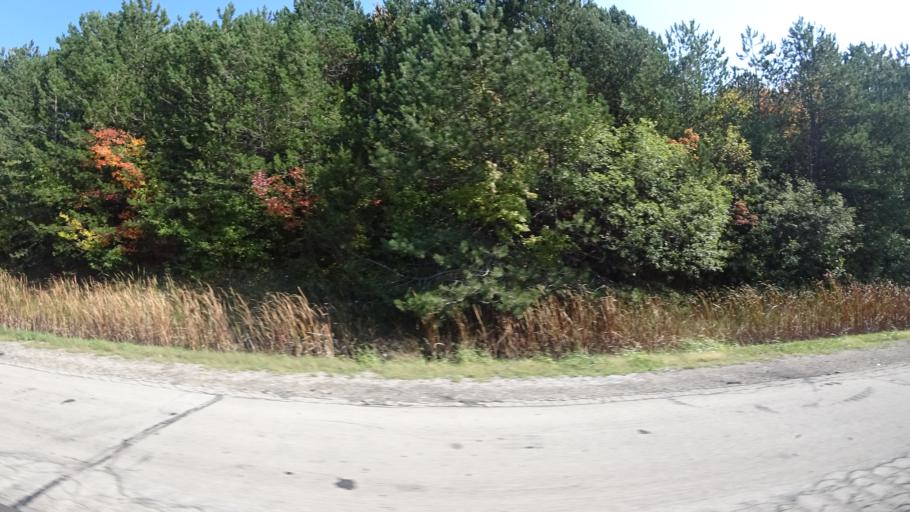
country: US
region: Michigan
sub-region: Washtenaw County
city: Ann Arbor
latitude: 42.2657
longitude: -83.7847
